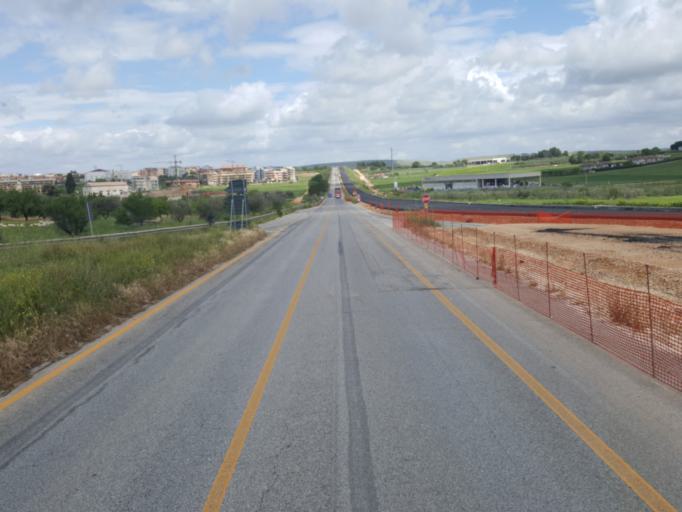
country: IT
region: Apulia
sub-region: Provincia di Bari
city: Altamura
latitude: 40.8251
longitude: 16.5707
